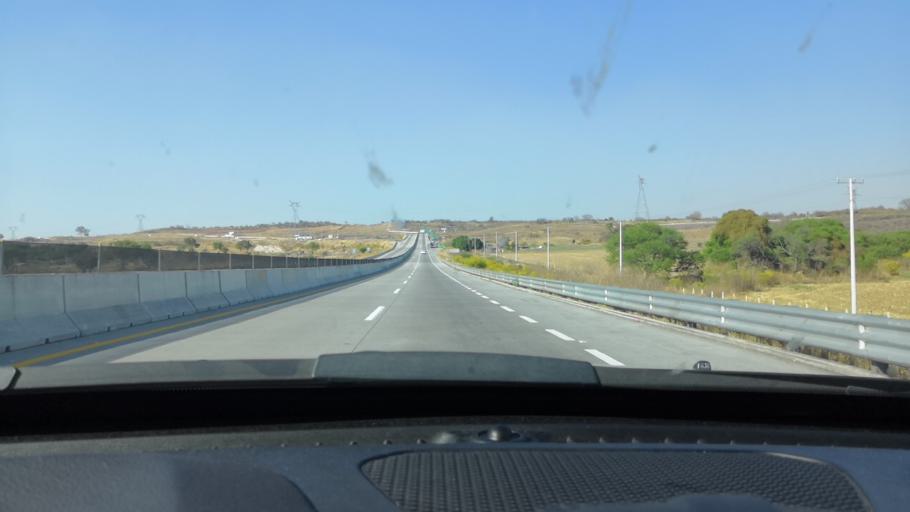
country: MX
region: Jalisco
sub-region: Zapotlanejo
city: La Mezquitera
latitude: 20.5776
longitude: -103.1006
